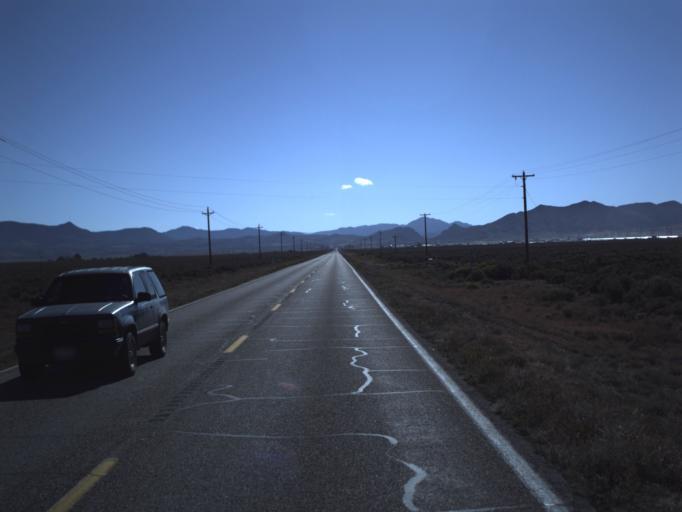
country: US
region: Utah
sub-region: Washington County
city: Enterprise
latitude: 37.6983
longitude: -113.6253
